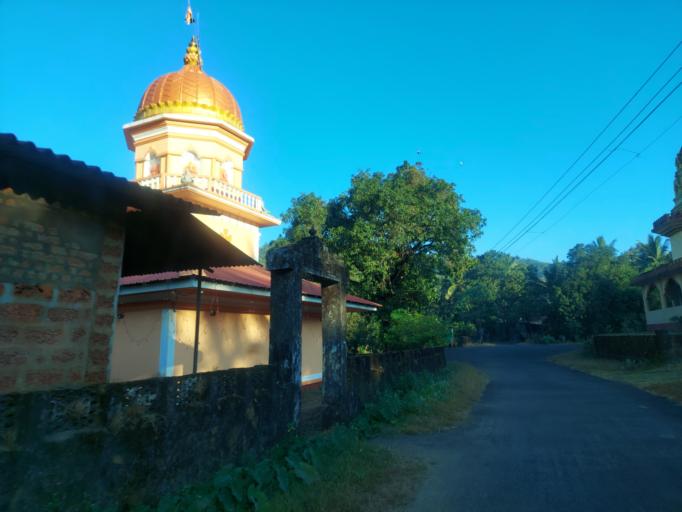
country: IN
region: Maharashtra
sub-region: Sindhudurg
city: Kudal
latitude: 16.0685
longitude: 73.8240
